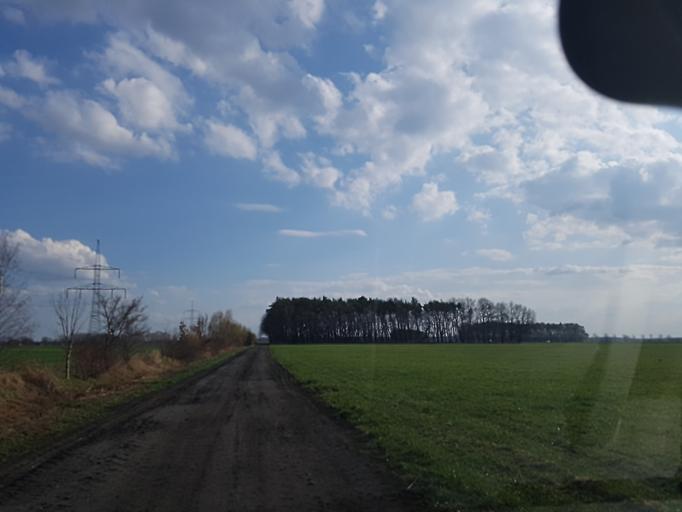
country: DE
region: Brandenburg
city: Schonborn
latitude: 51.6052
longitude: 13.5270
